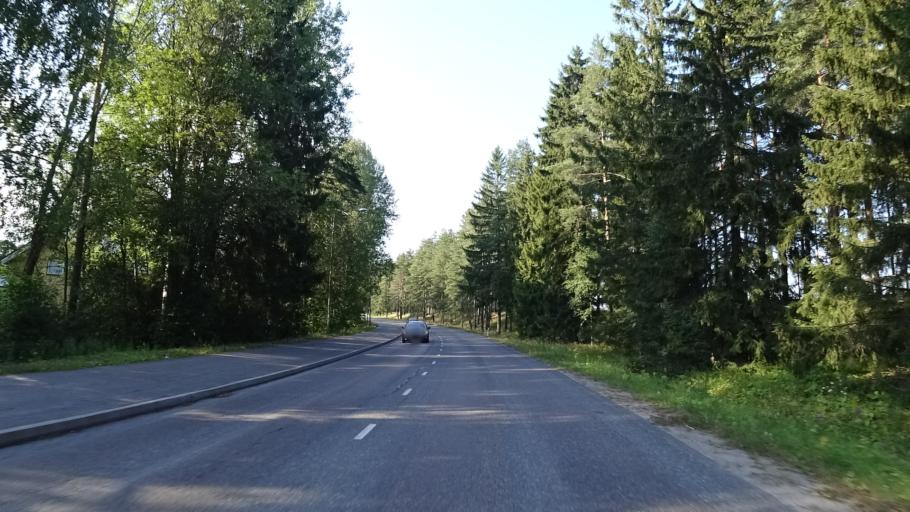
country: FI
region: South Karelia
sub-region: Imatra
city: Imatra
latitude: 61.1800
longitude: 28.7818
